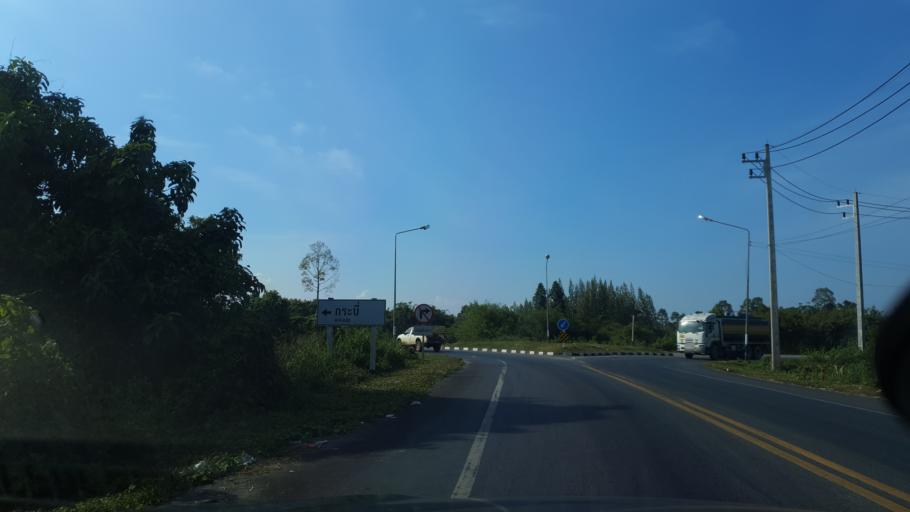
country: TH
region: Surat Thani
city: Ban Na Doem
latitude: 8.9360
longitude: 99.2688
